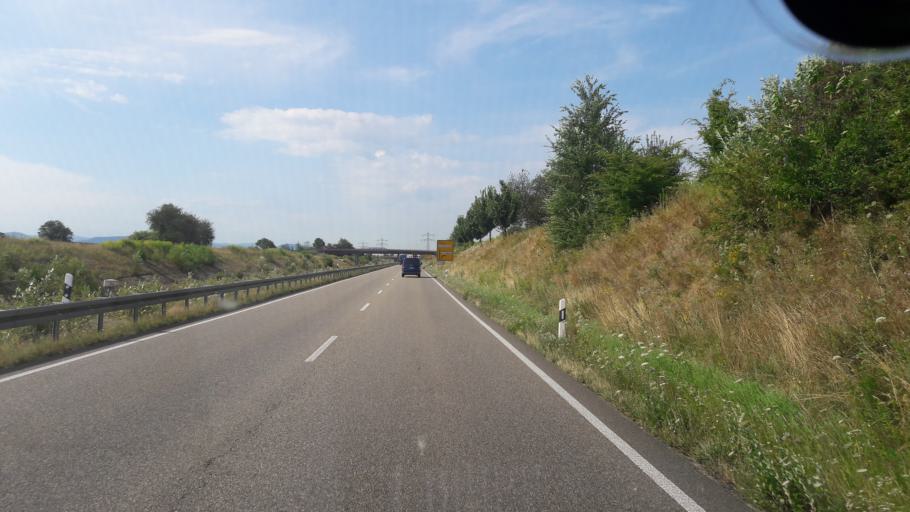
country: DE
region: Baden-Wuerttemberg
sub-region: Karlsruhe Region
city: Bietigheim
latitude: 48.9148
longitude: 8.2677
